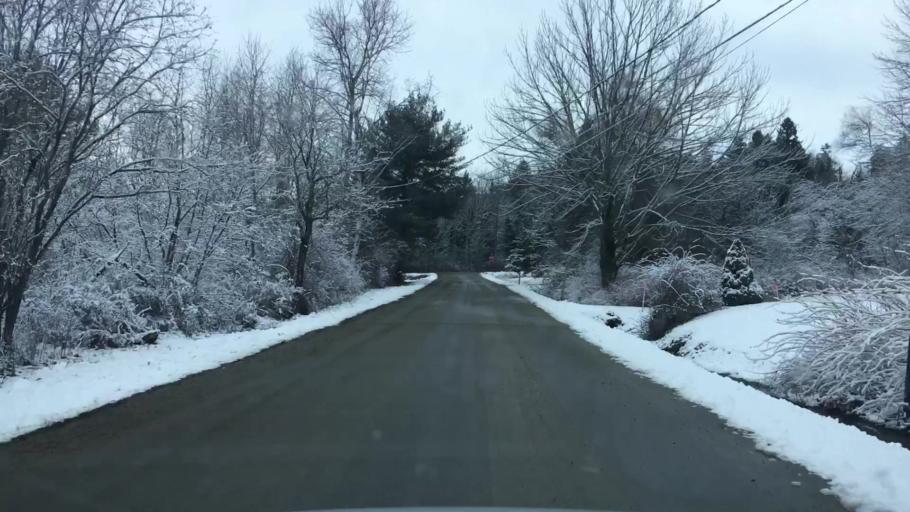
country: US
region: Maine
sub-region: Knox County
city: Owls Head
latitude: 44.0691
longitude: -69.0730
